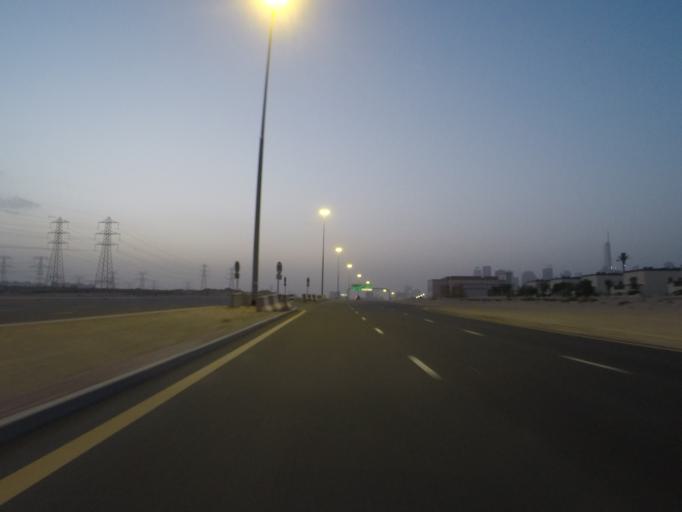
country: AE
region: Dubai
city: Dubai
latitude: 25.0478
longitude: 55.1471
